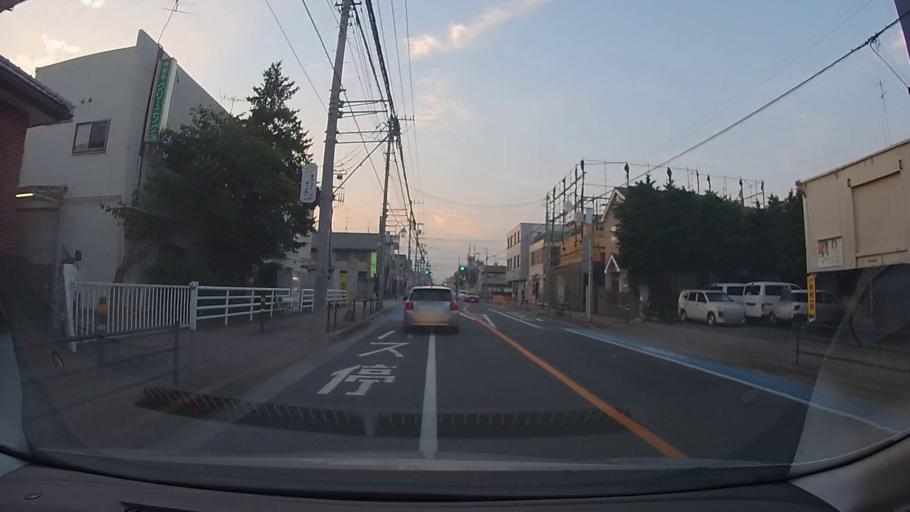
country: JP
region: Kanagawa
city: Minami-rinkan
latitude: 35.4836
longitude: 139.4507
